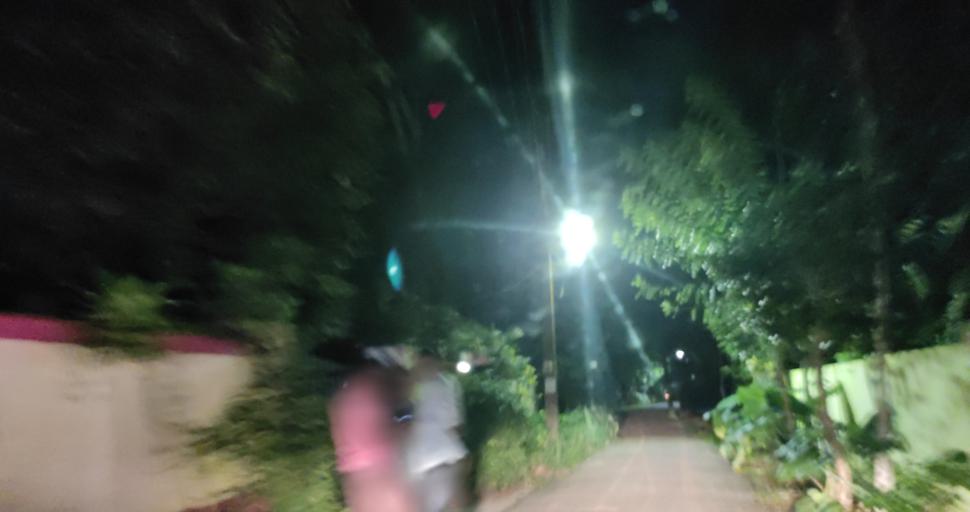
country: IN
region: Kerala
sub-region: Alappuzha
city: Shertallai
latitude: 9.6166
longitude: 76.3366
